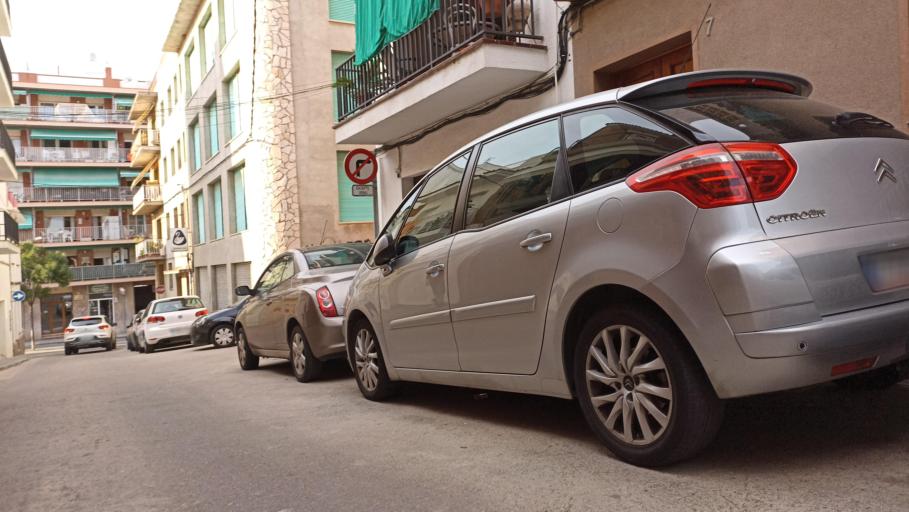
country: ES
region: Catalonia
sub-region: Provincia de Barcelona
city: Canet de Mar
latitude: 41.5880
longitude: 2.5791
